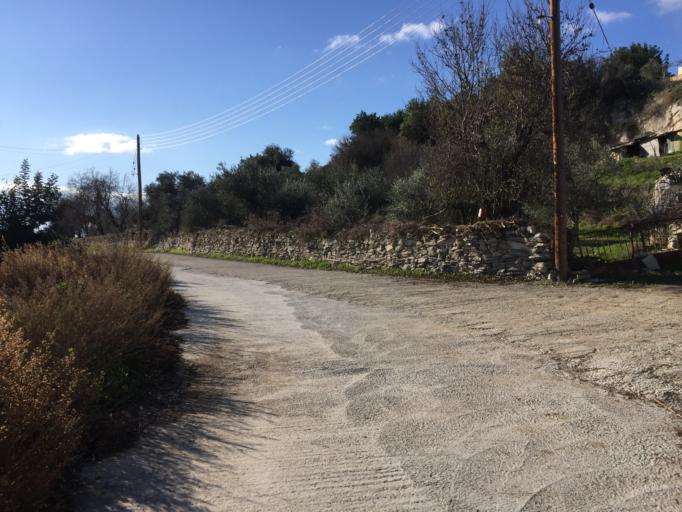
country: CY
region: Pafos
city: Mesogi
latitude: 34.8447
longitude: 32.5031
